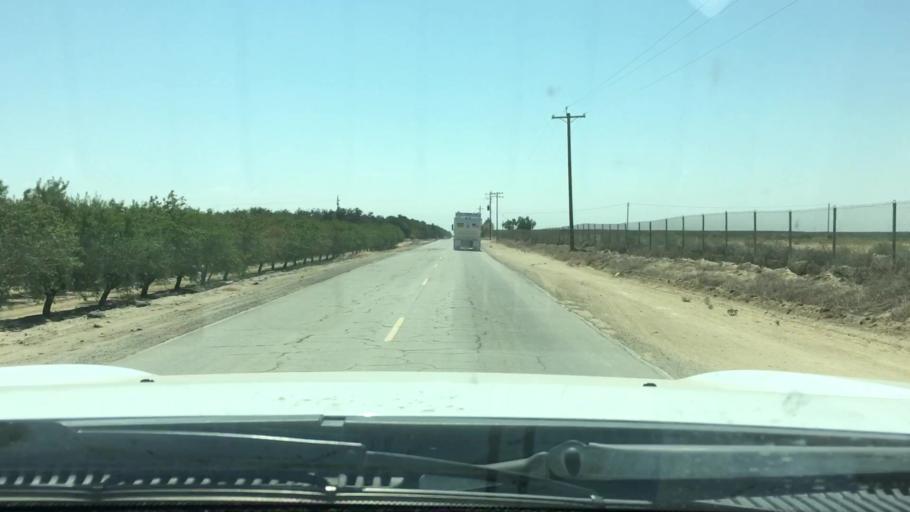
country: US
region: California
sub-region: Kern County
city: Wasco
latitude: 35.5095
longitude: -119.4033
